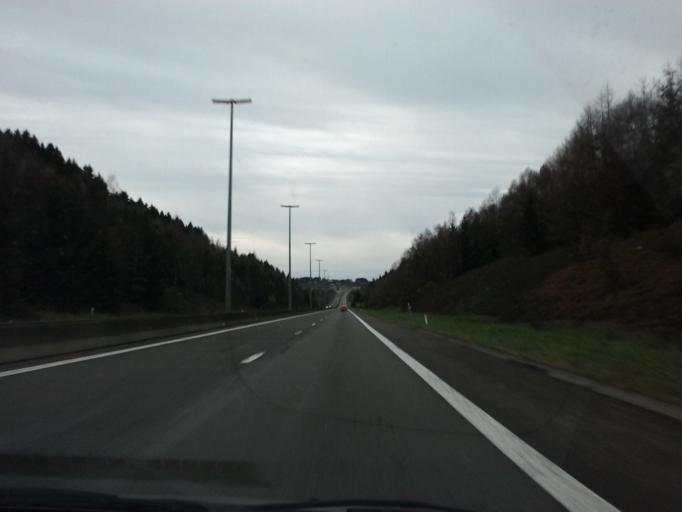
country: BE
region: Wallonia
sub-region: Province du Luxembourg
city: Manhay
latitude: 50.3460
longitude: 5.6863
